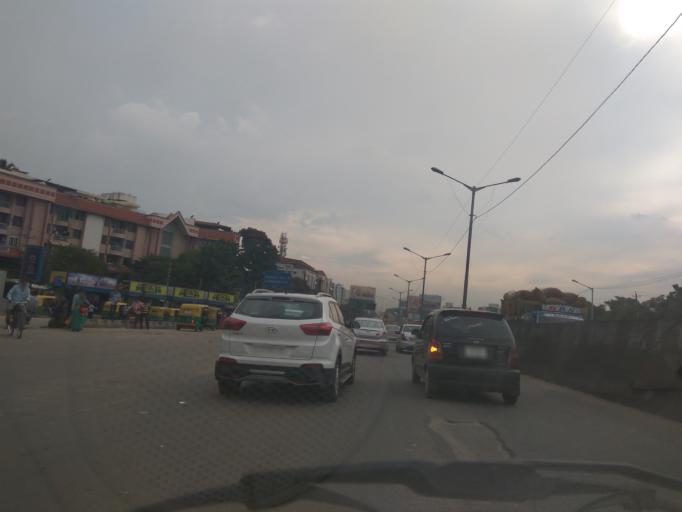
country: IN
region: Karnataka
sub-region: Bangalore Urban
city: Bangalore
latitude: 12.9966
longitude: 77.6690
